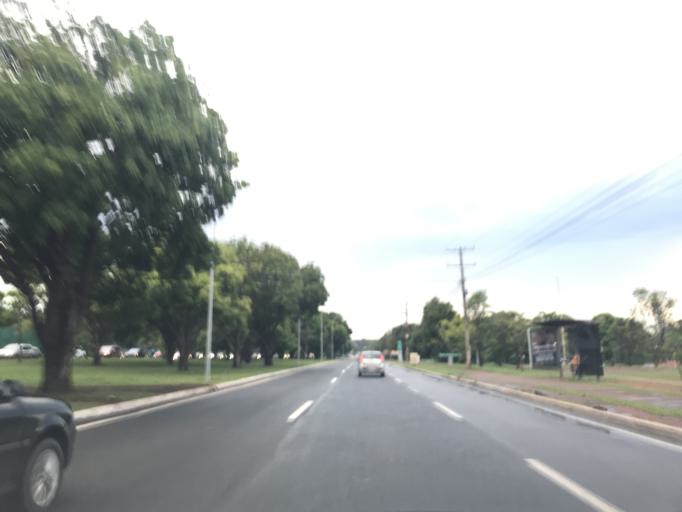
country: BR
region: Federal District
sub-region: Brasilia
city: Brasilia
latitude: -15.8467
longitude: -47.8734
